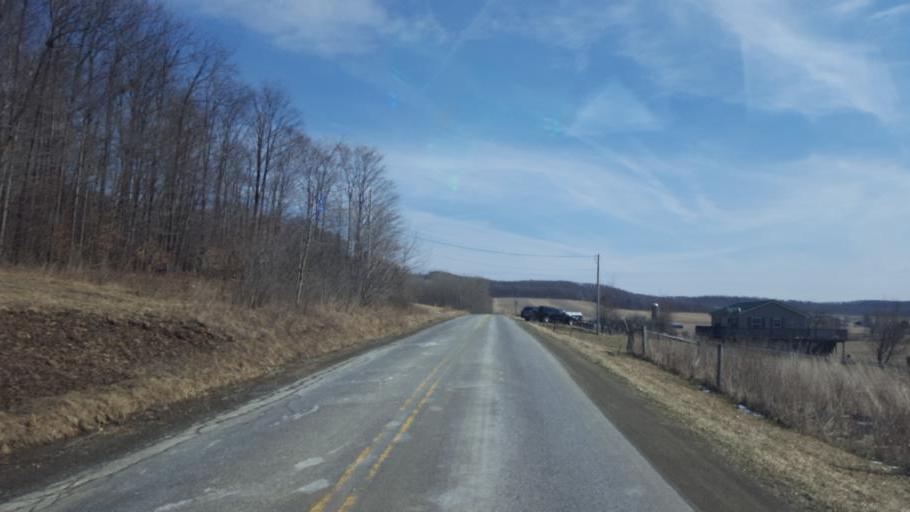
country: US
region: Pennsylvania
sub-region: Potter County
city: Galeton
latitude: 41.8949
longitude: -77.7533
